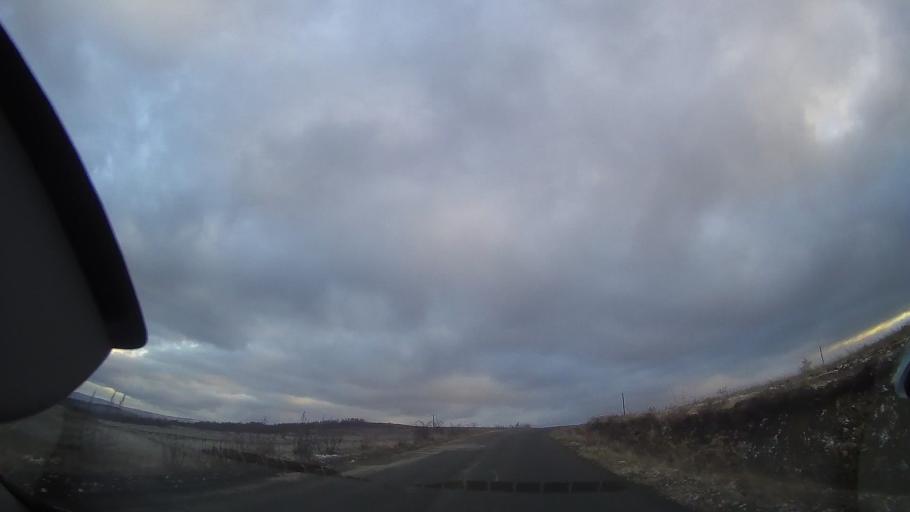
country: RO
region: Cluj
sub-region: Comuna Manastireni
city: Manastireni
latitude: 46.7787
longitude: 23.0556
